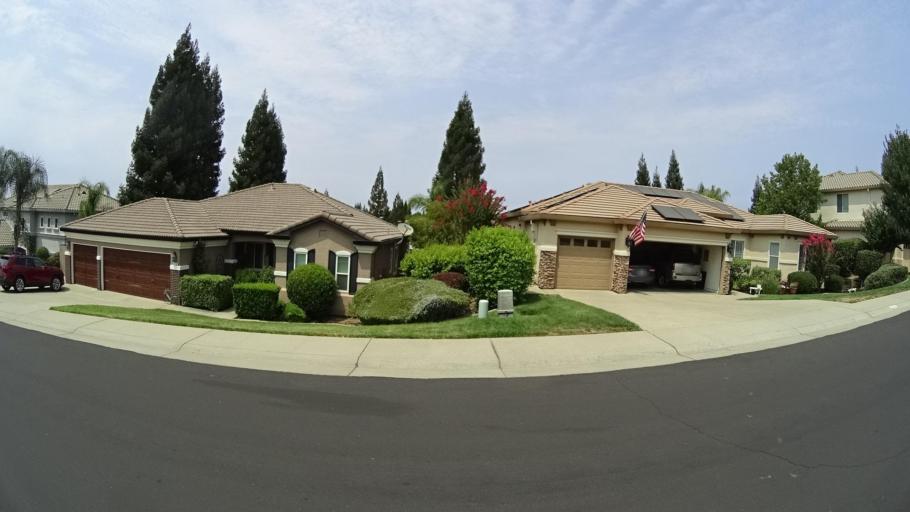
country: US
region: California
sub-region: Placer County
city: Rocklin
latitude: 38.7735
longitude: -121.2197
